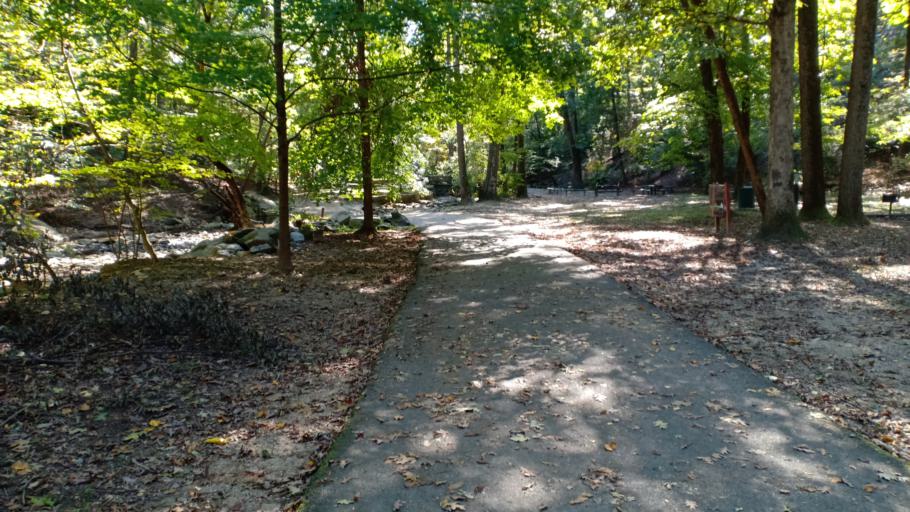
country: US
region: Virginia
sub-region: Arlington County
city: Arlington
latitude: 38.8713
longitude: -77.1169
